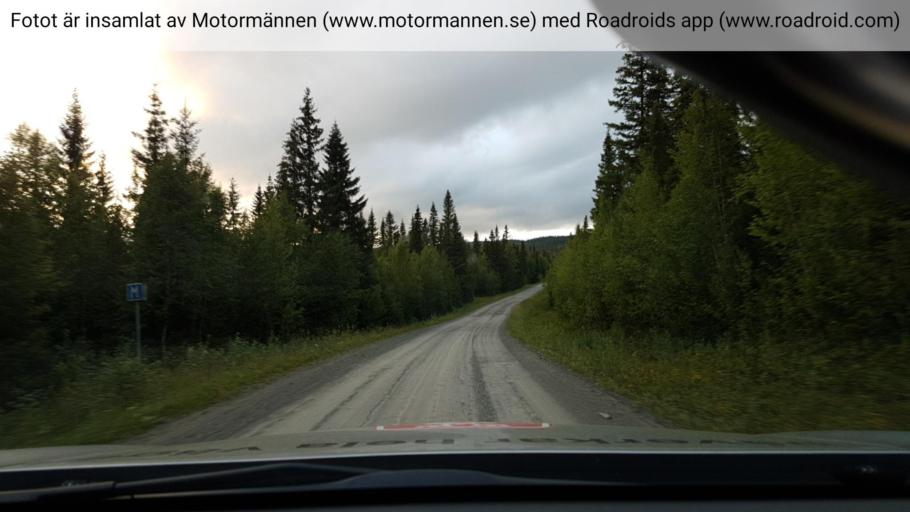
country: SE
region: Vaesterbotten
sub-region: Vilhelmina Kommun
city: Sjoberg
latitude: 65.5476
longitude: 15.4166
